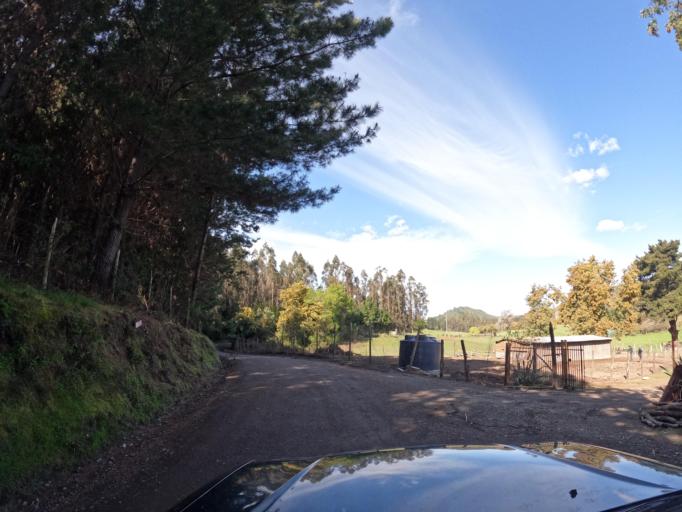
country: CL
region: Biobio
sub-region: Provincia de Concepcion
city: Chiguayante
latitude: -37.0629
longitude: -72.8965
